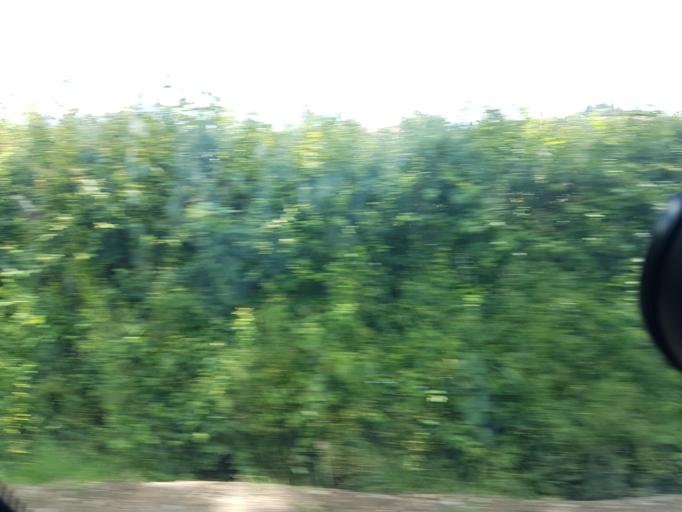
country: FR
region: Bourgogne
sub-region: Departement de Saone-et-Loire
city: Epinac
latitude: 46.9752
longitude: 4.4920
